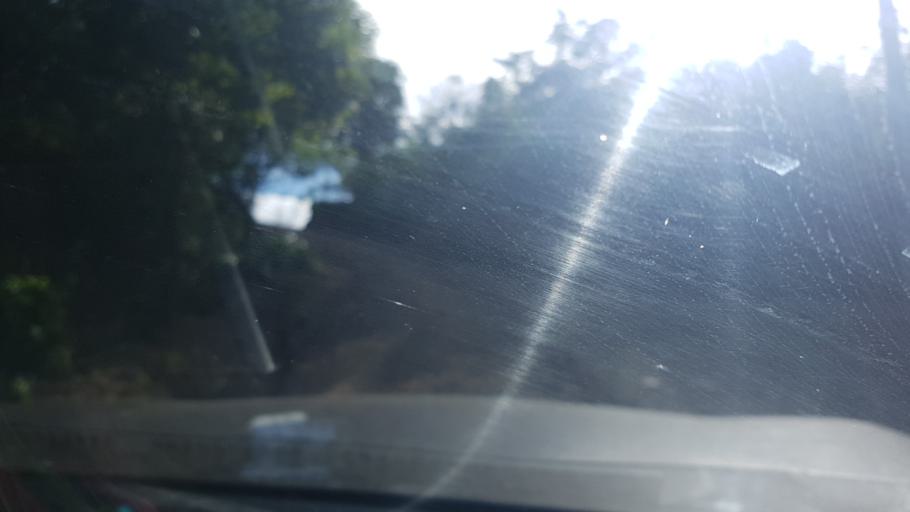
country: NI
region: Nueva Segovia
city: Ocotal
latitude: 13.6115
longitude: -86.4508
